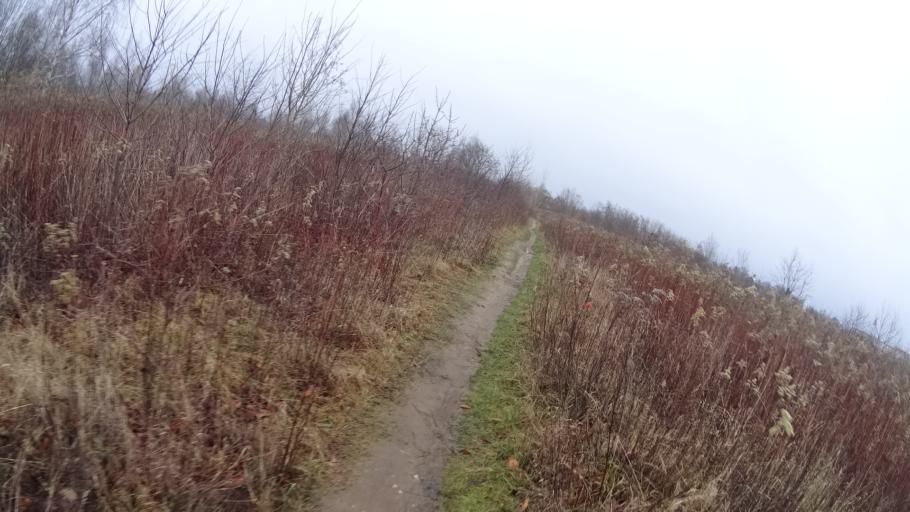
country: PL
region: Masovian Voivodeship
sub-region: Warszawa
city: Wilanow
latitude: 52.1547
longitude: 21.0869
